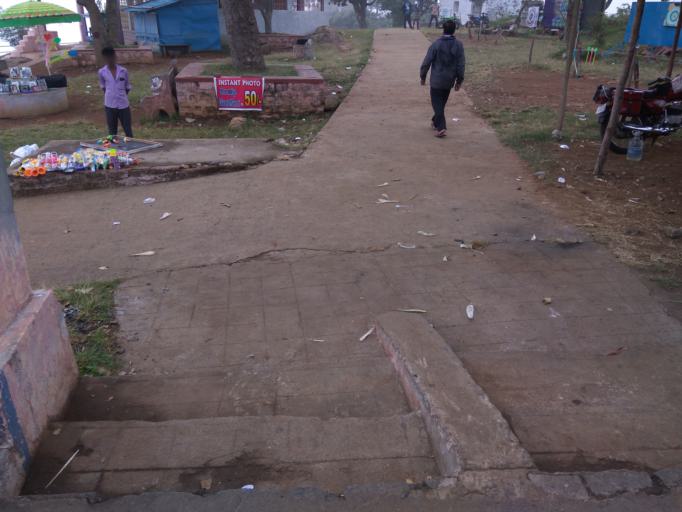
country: IN
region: Tamil Nadu
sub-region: Salem
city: Salem
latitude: 11.7668
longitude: 78.2393
